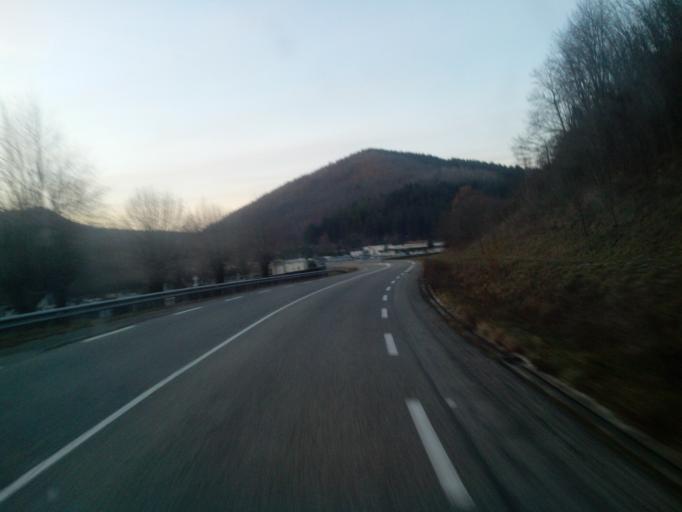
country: FR
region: Midi-Pyrenees
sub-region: Departement de l'Ariege
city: Saint-Paul-de-Jarrat
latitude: 42.9164
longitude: 1.6581
